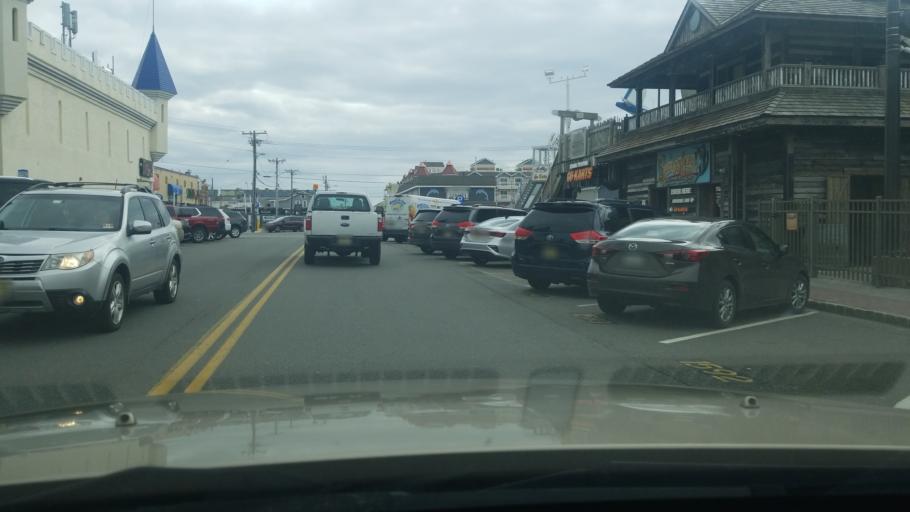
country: US
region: New Jersey
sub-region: Ocean County
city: Seaside Heights
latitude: 39.9430
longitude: -74.0710
